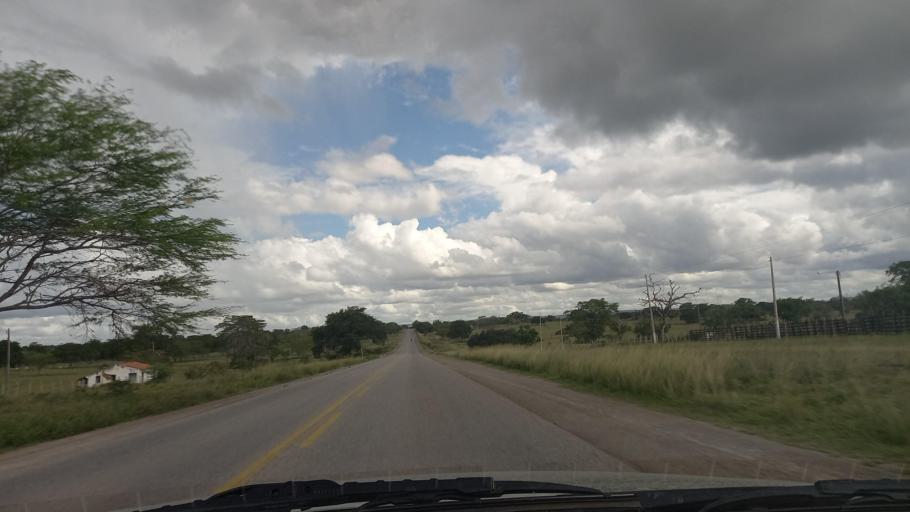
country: BR
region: Pernambuco
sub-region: Cachoeirinha
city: Cachoeirinha
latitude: -8.5292
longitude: -36.2626
